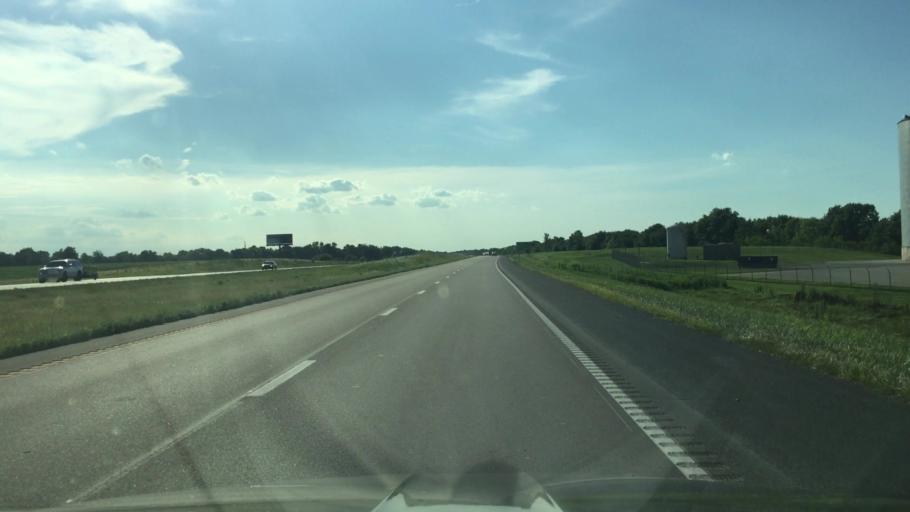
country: US
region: Missouri
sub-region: Pettis County
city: La Monte
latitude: 38.7498
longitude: -93.3457
